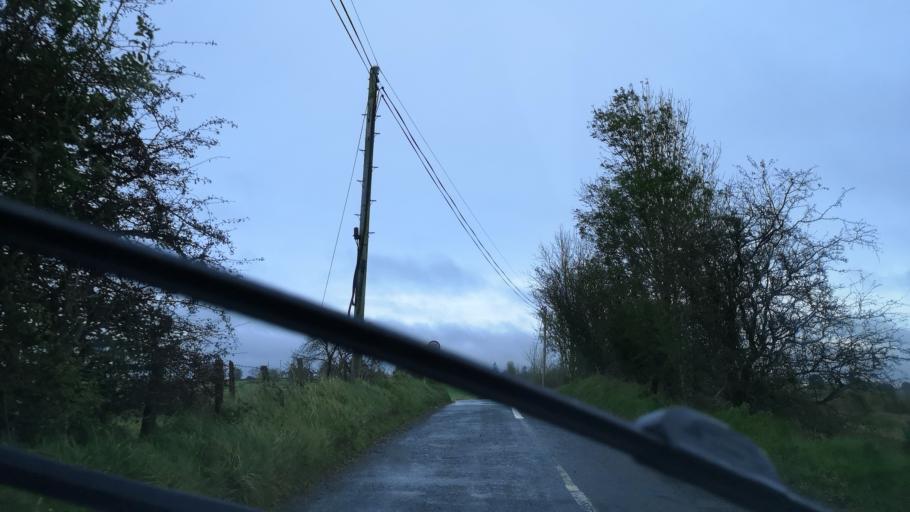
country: IE
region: Connaught
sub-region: Maigh Eo
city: Ballyhaunis
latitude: 53.7710
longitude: -8.7606
